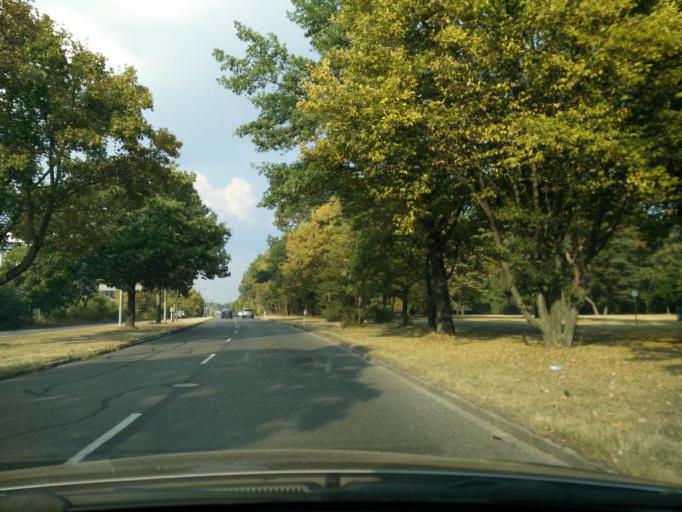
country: DE
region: Bavaria
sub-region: Regierungsbezirk Mittelfranken
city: Wendelstein
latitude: 49.4056
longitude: 11.1333
